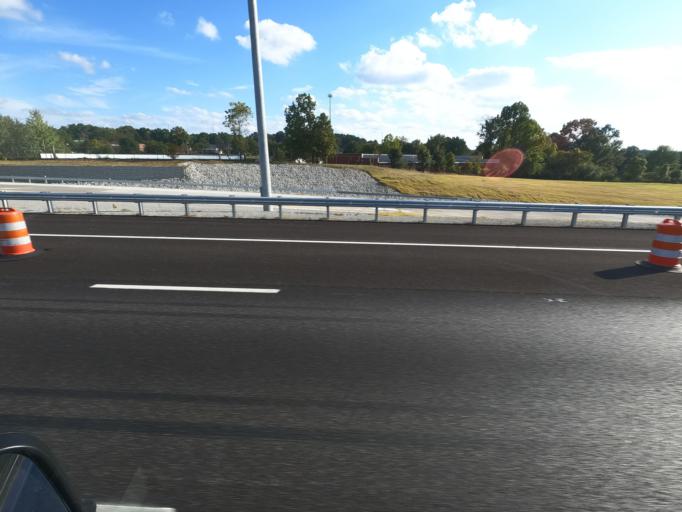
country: US
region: Tennessee
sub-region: Madison County
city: Jackson
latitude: 35.6725
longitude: -88.8274
